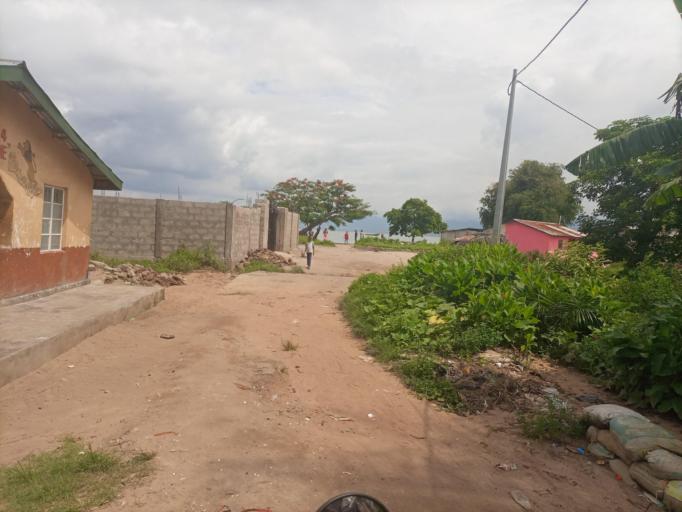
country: SL
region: Western Area
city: Freetown
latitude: 8.5233
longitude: -13.1451
